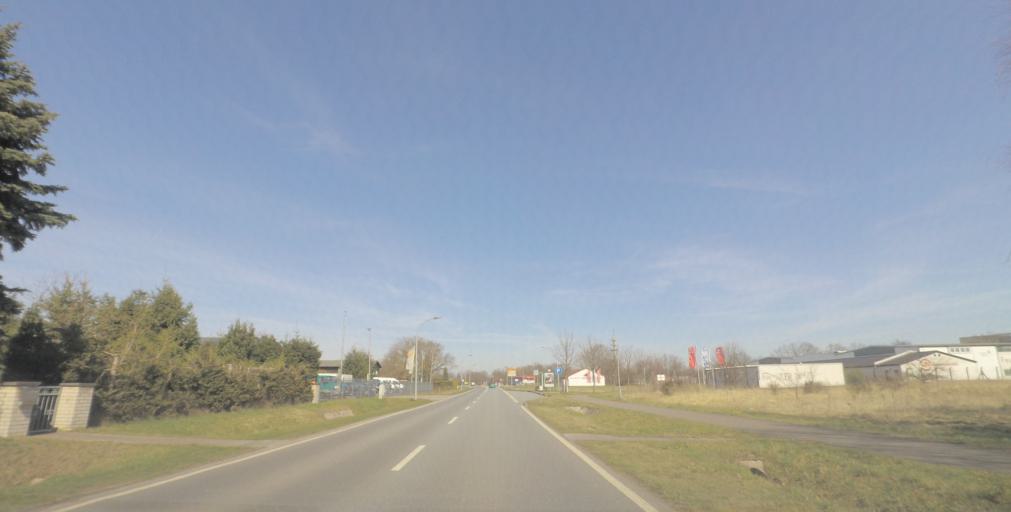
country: DE
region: Brandenburg
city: Neuruppin
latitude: 52.8846
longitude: 12.7950
